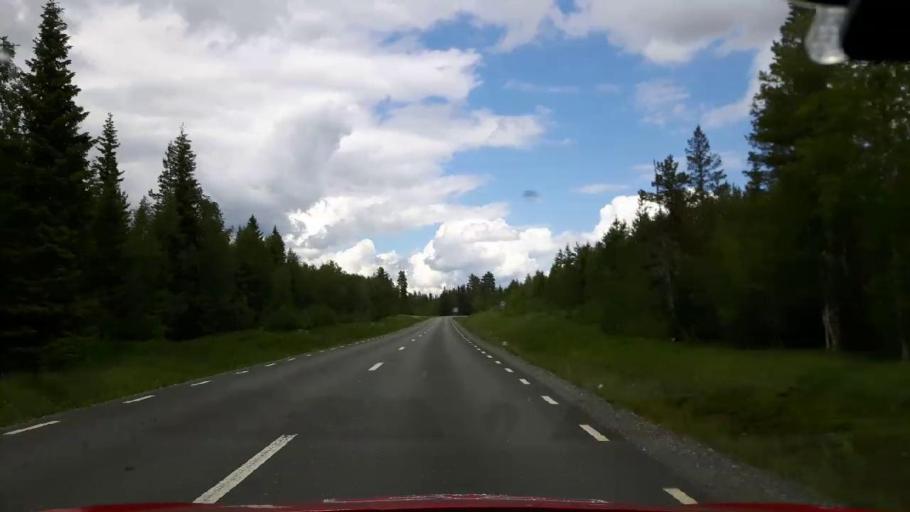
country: SE
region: Jaemtland
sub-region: Krokoms Kommun
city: Krokom
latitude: 63.5879
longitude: 14.2945
